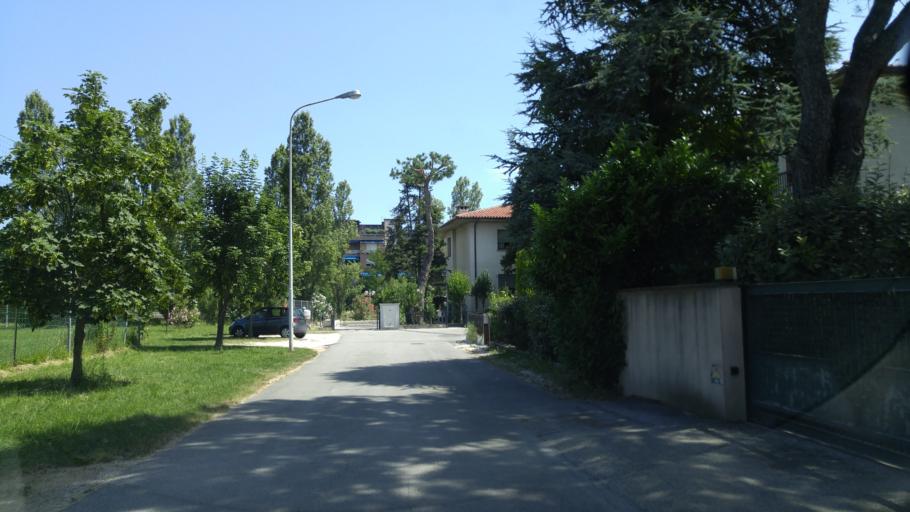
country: IT
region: The Marches
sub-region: Provincia di Pesaro e Urbino
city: Centinarola
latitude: 43.8307
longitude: 13.0041
